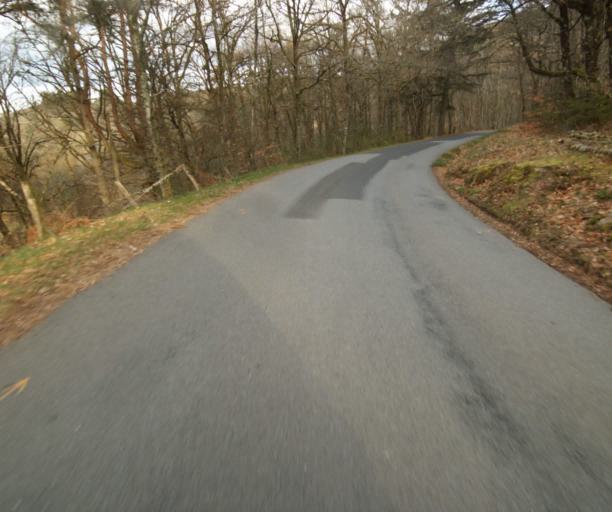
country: FR
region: Limousin
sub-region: Departement de la Correze
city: Correze
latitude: 45.4167
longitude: 1.8993
